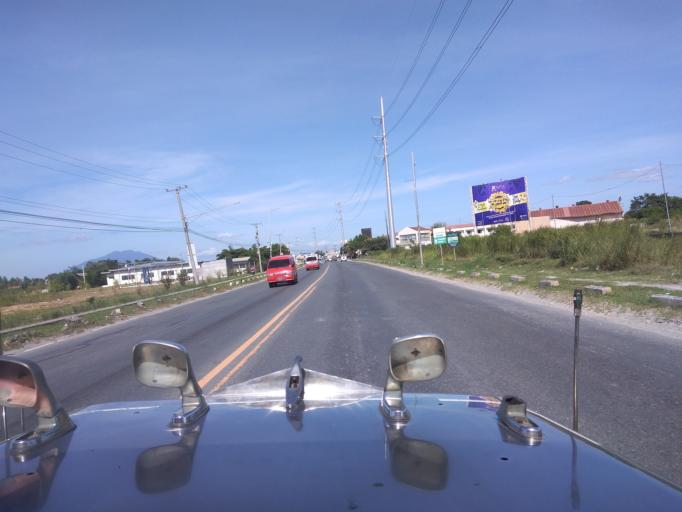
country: PH
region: Central Luzon
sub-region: Province of Pampanga
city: San Juan
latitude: 15.0214
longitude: 120.6690
